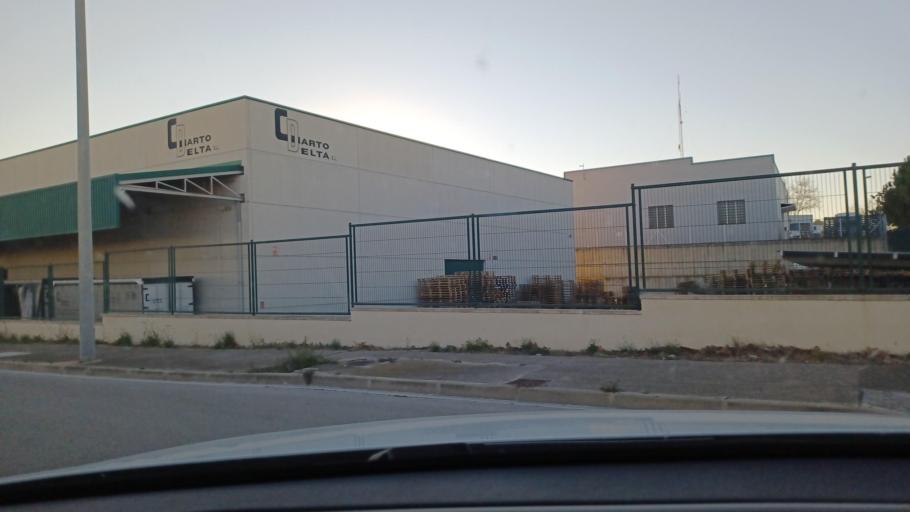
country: ES
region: Catalonia
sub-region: Provincia de Tarragona
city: Amposta
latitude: 40.7044
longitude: 0.5605
